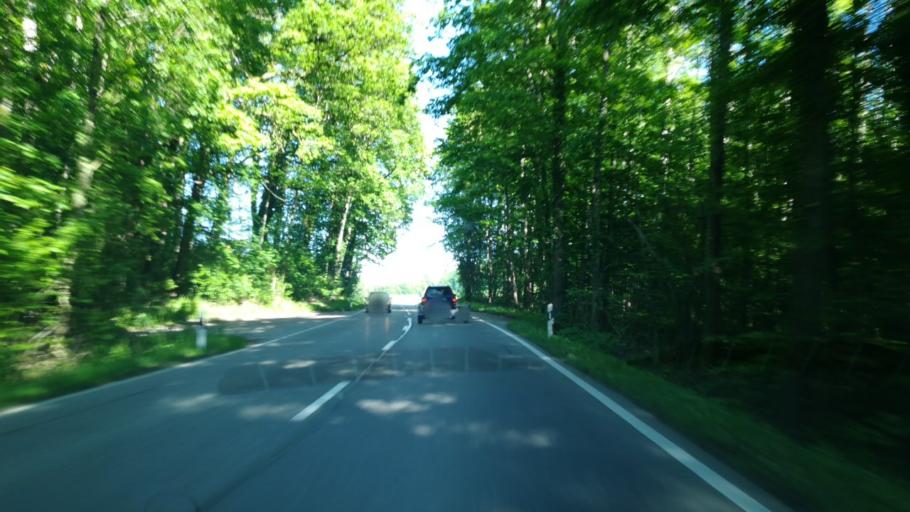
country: CH
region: Thurgau
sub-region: Frauenfeld District
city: Wagenhausen
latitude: 47.6577
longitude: 8.8035
